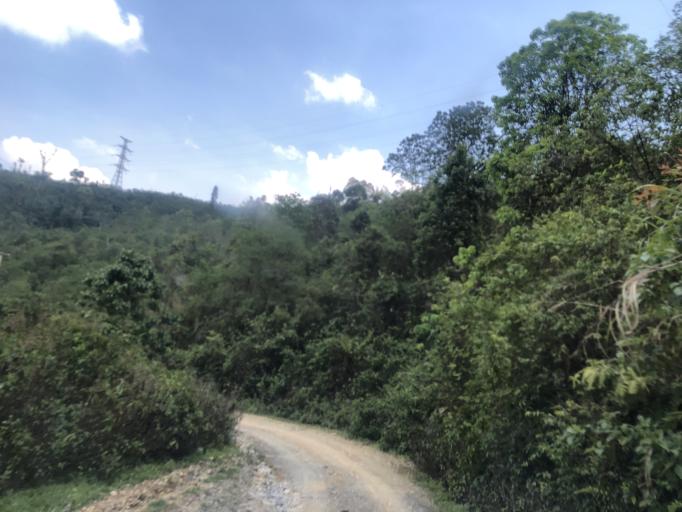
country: LA
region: Phongsali
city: Phongsali
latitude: 21.3895
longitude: 102.1978
